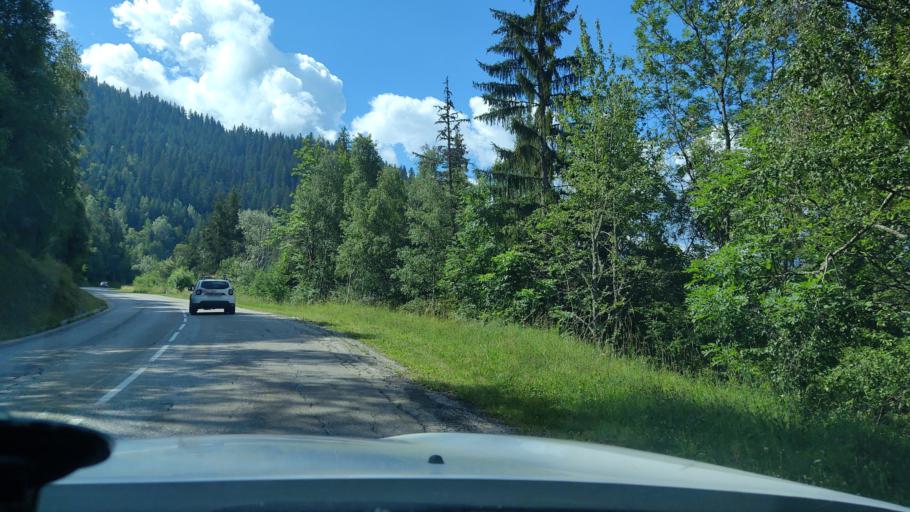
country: FR
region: Rhone-Alpes
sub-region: Departement de la Savoie
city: Bourg-Saint-Maurice
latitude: 45.5970
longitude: 6.7810
